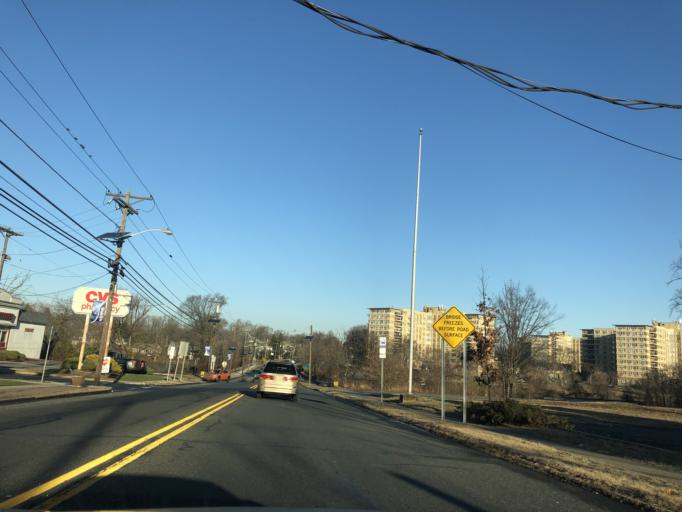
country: US
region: New Jersey
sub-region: Camden County
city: Oaklyn
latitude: 39.9069
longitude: -75.0809
